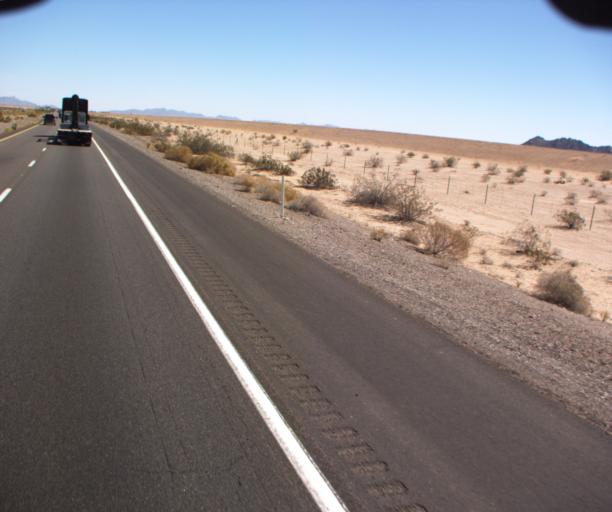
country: US
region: Arizona
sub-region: Yuma County
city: Wellton
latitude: 32.6772
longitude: -114.0423
